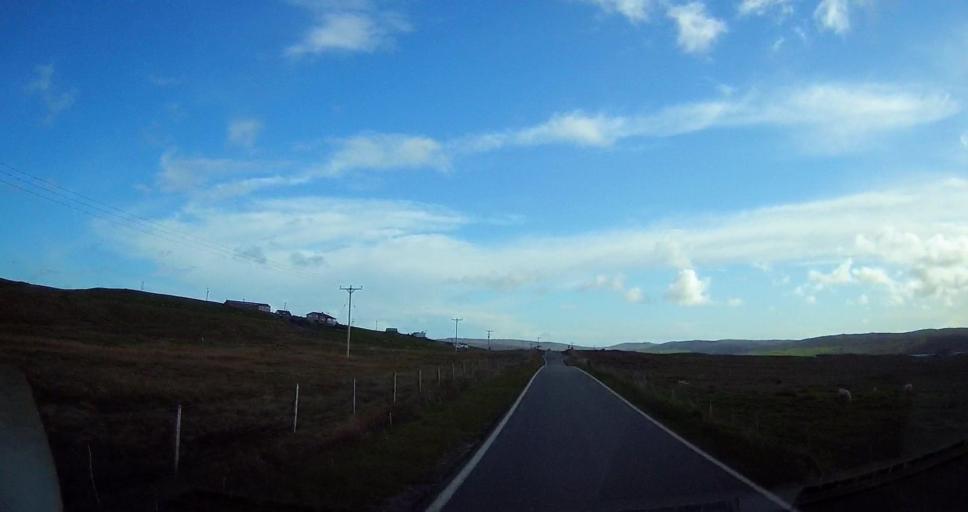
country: GB
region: Scotland
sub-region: Shetland Islands
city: Shetland
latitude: 60.3592
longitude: -1.1445
